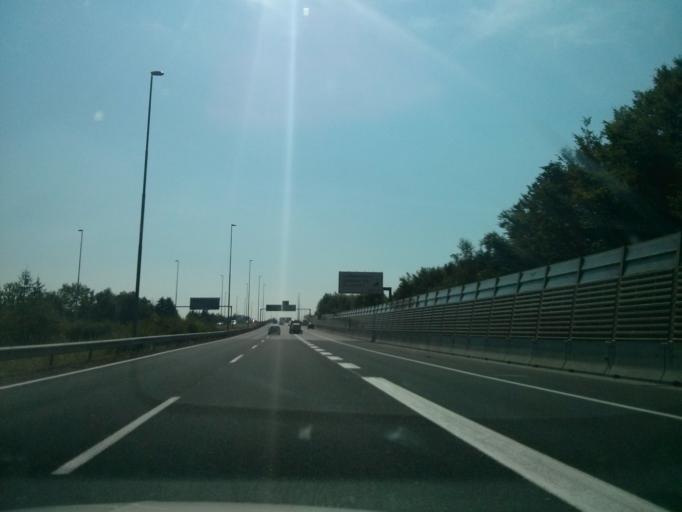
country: SI
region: Brezovica
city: Vnanje Gorice
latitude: 46.0368
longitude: 14.4563
